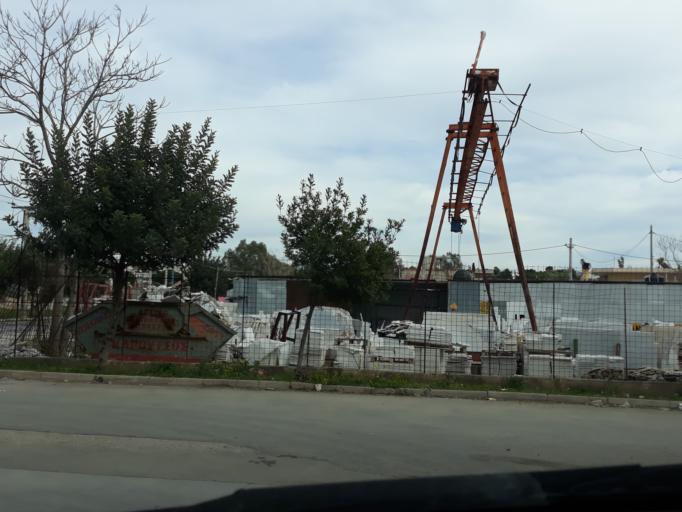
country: GR
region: Attica
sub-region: Nomarchia Dytikis Attikis
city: Zefyri
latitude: 38.0798
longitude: 23.7150
